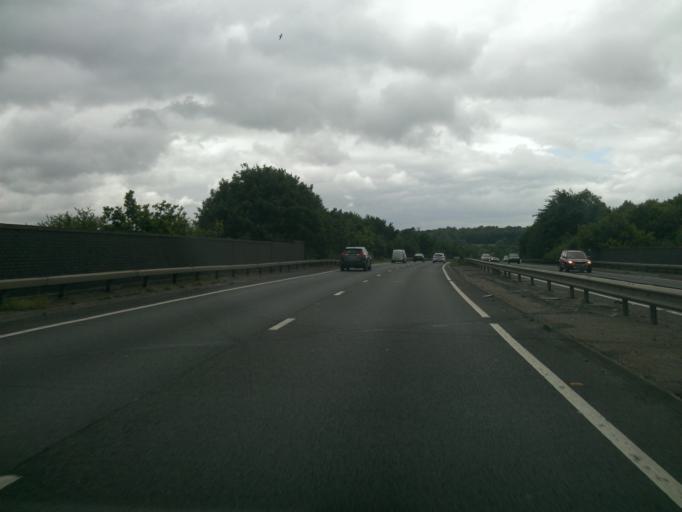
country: GB
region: England
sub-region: Essex
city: West Bergholt
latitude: 51.9018
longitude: 0.8654
